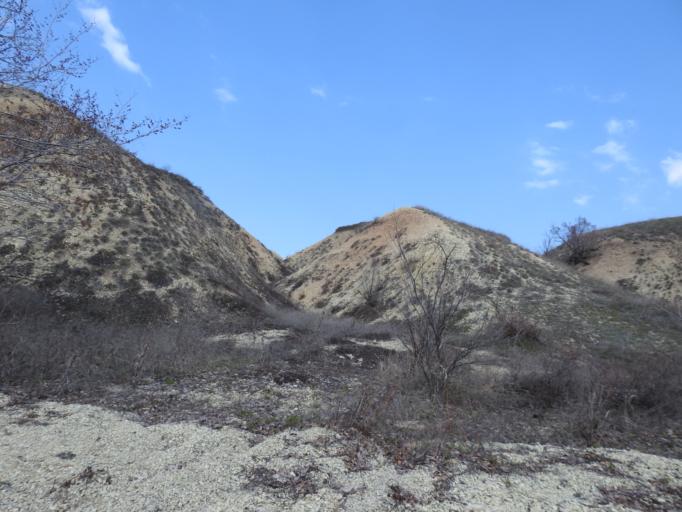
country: RU
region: Saratov
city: Voskresenskoye
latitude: 51.7976
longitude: 46.8917
